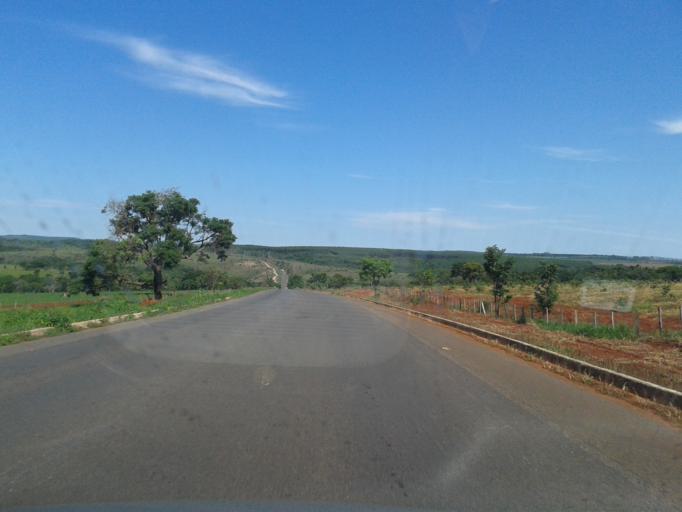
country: BR
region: Goias
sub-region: Bela Vista De Goias
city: Bela Vista de Goias
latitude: -17.1785
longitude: -48.7183
